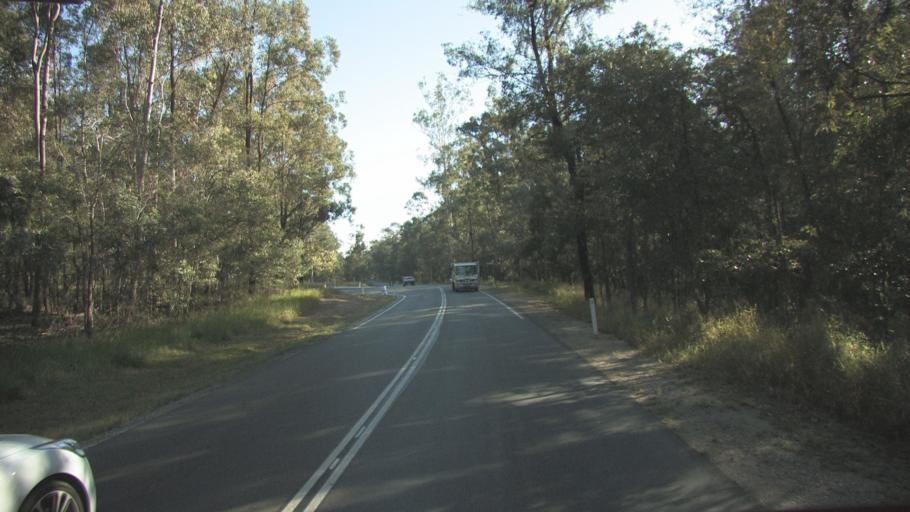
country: AU
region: Queensland
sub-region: Ipswich
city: Springfield Lakes
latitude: -27.7002
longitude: 152.9724
